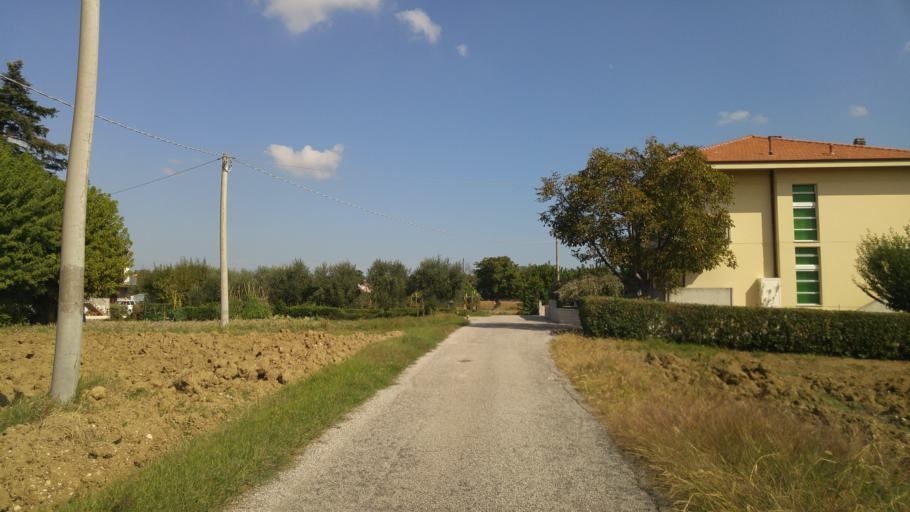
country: IT
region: The Marches
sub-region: Provincia di Pesaro e Urbino
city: Lucrezia
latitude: 43.7698
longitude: 12.9417
